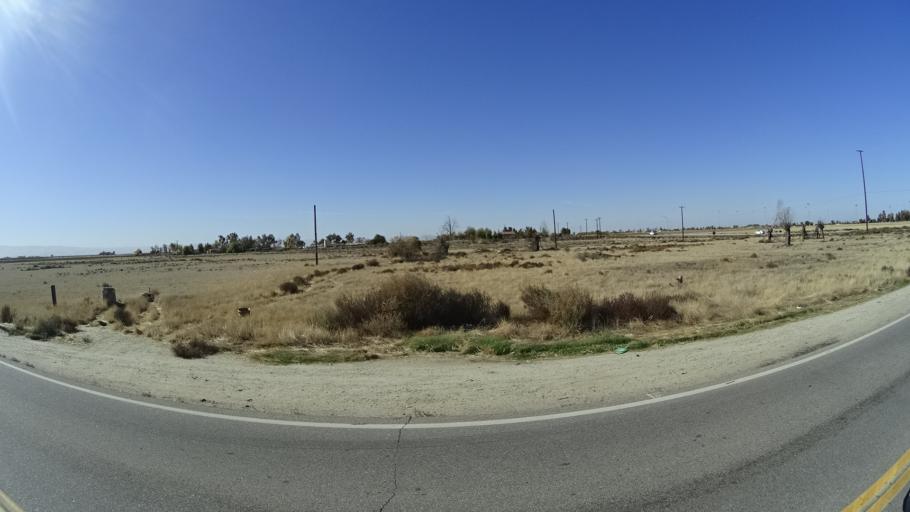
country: US
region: California
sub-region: Kern County
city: Greenfield
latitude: 35.2660
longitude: -119.0744
